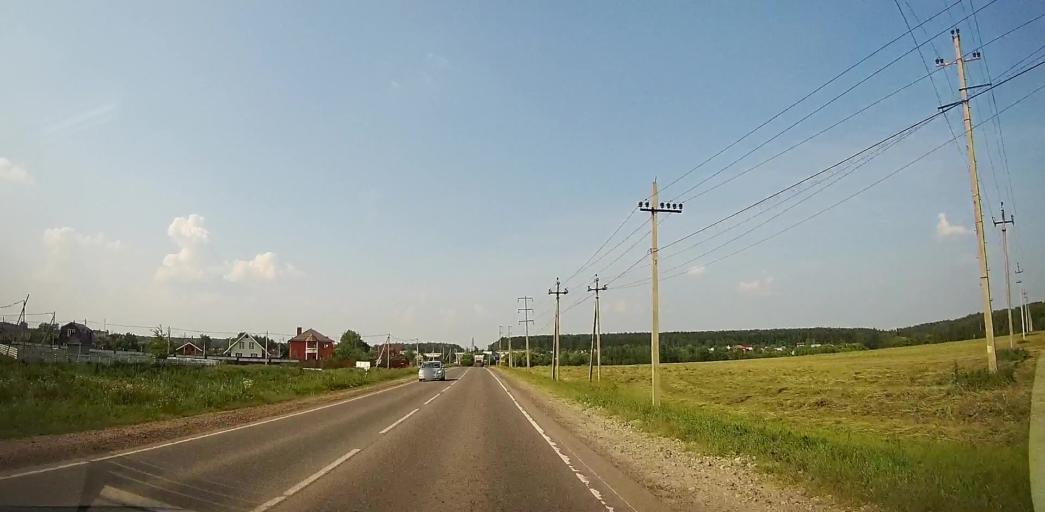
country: RU
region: Moskovskaya
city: Barybino
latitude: 55.2715
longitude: 37.9157
